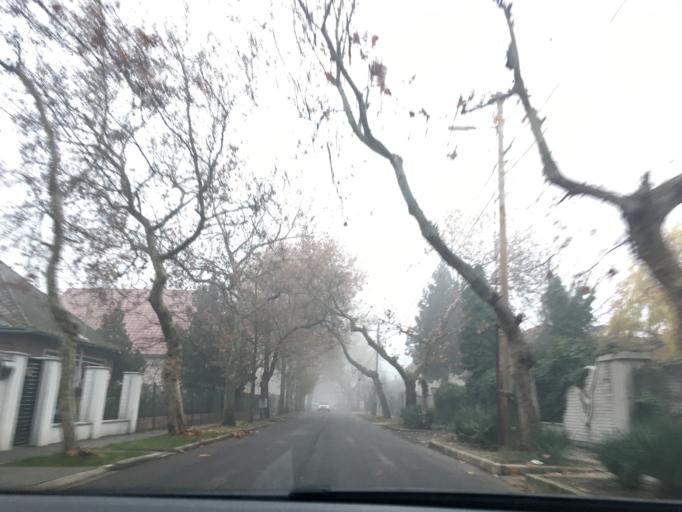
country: HU
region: Hajdu-Bihar
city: Debrecen
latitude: 47.5364
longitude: 21.6492
